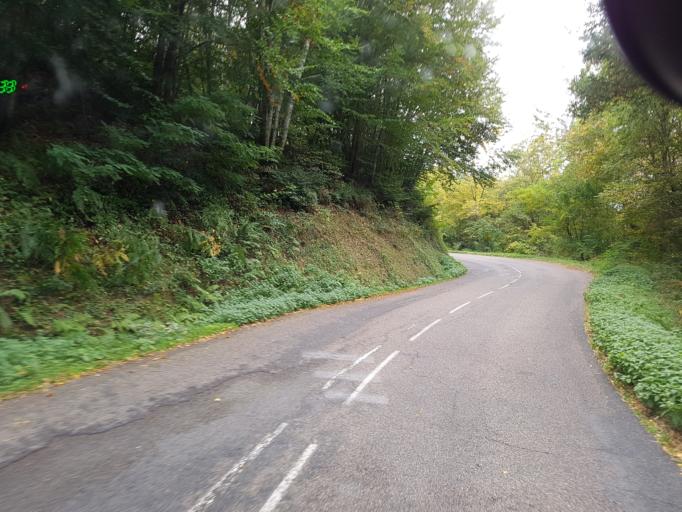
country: FR
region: Rhone-Alpes
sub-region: Departement du Rhone
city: Aveize
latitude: 45.6729
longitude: 4.4442
